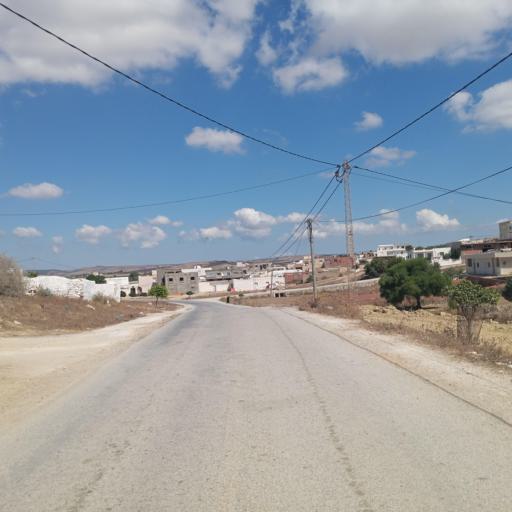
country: TN
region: Nabul
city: Qulaybiyah
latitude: 36.8579
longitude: 11.0330
